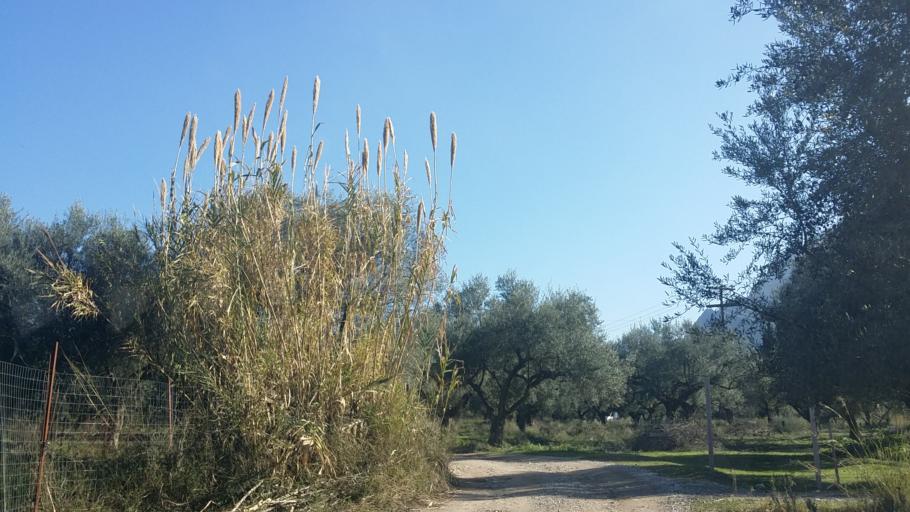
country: GR
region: West Greece
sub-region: Nomos Achaias
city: Temeni
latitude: 38.1924
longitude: 22.1861
